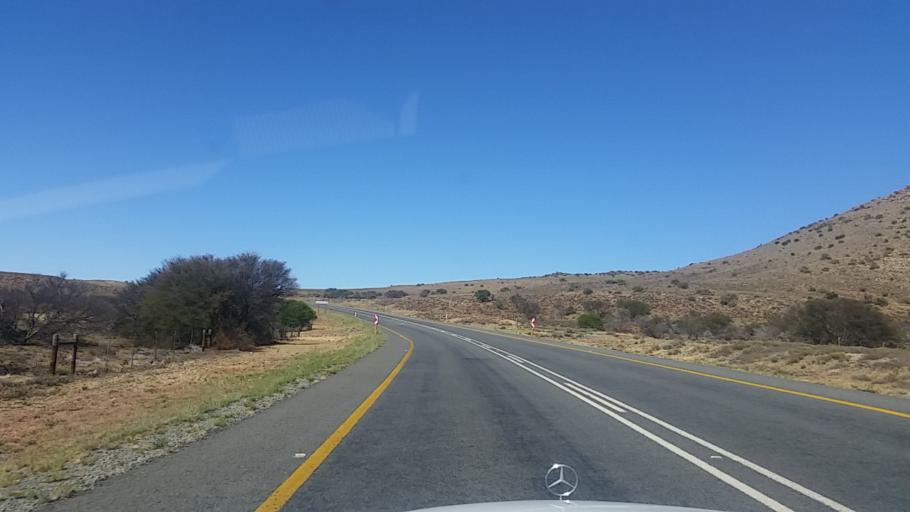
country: ZA
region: Eastern Cape
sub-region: Cacadu District Municipality
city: Graaff-Reinet
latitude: -31.9457
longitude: 24.7272
